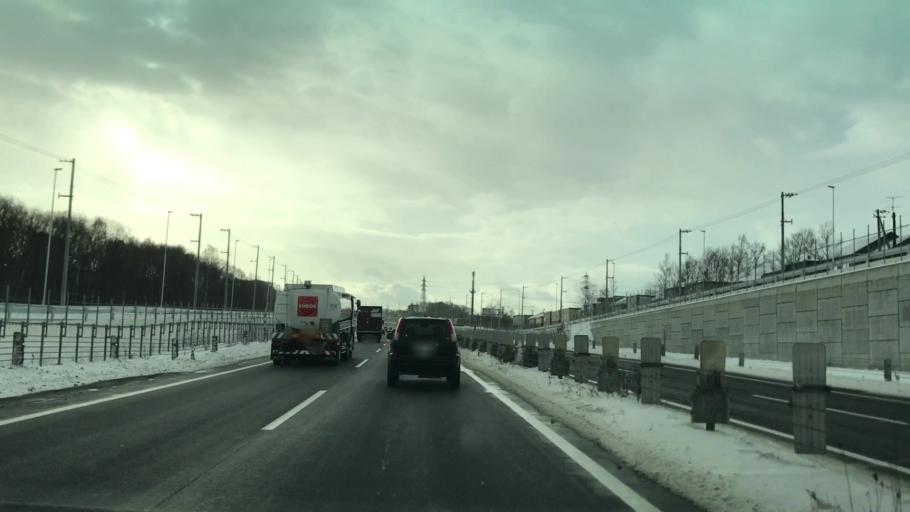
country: JP
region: Hokkaido
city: Kitahiroshima
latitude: 42.9902
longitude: 141.4698
